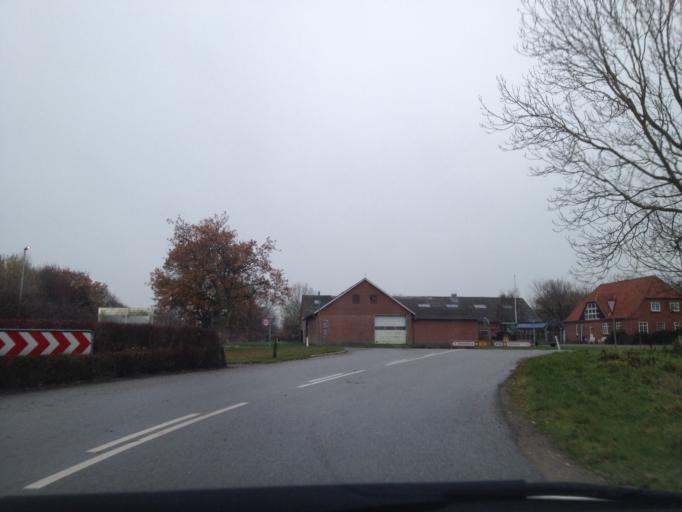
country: DK
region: South Denmark
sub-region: Tonder Kommune
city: Sherrebek
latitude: 55.0856
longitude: 8.7247
